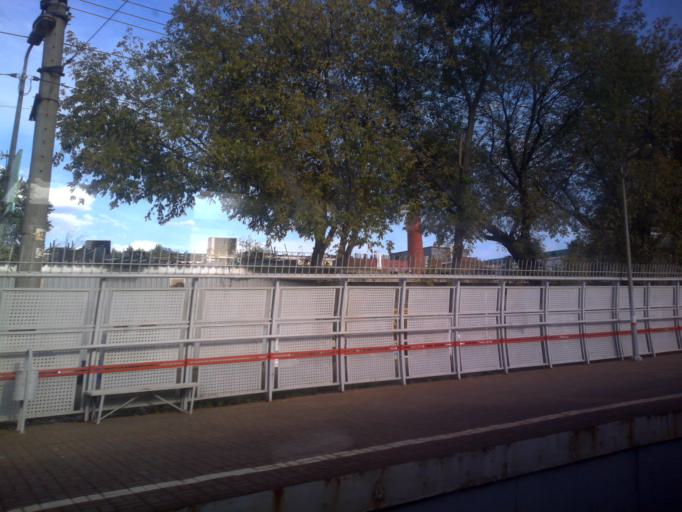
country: RU
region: Moscow
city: Kotlovka
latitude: 55.6812
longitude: 37.6213
